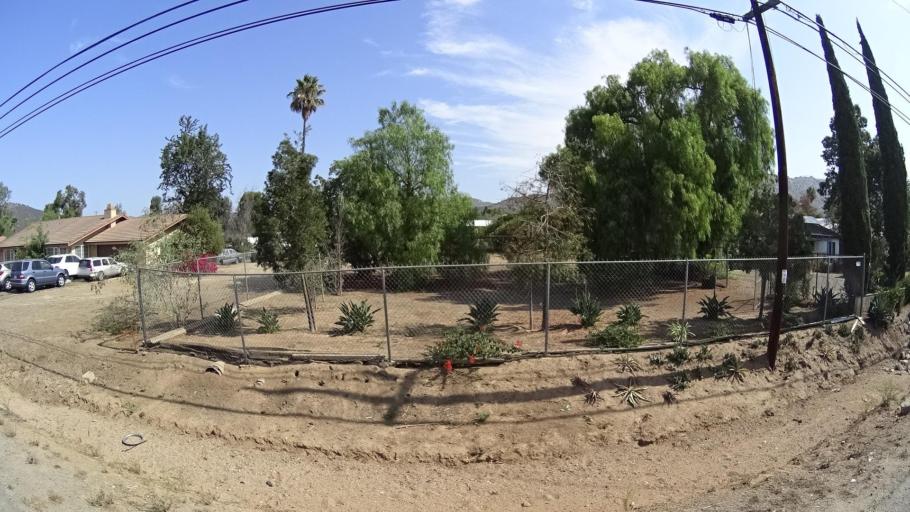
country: US
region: California
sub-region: San Diego County
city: San Marcos
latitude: 33.1788
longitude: -117.1496
